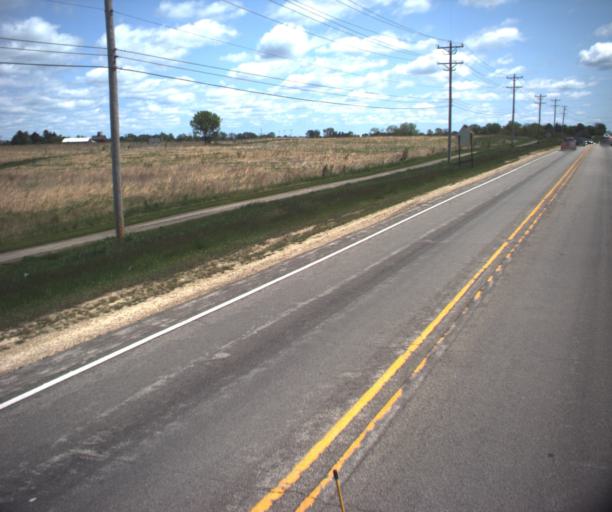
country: US
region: Illinois
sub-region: Kane County
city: Batavia
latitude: 41.8649
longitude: -88.3678
